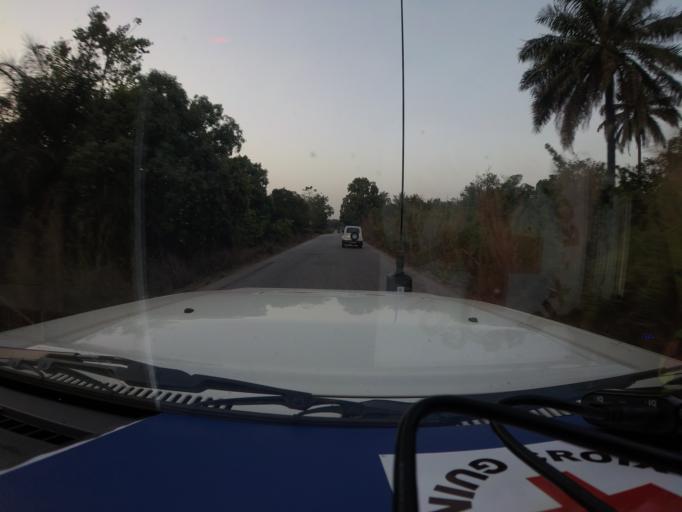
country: GN
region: Kindia
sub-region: Kindia
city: Kindia
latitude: 9.8819
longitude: -13.0549
